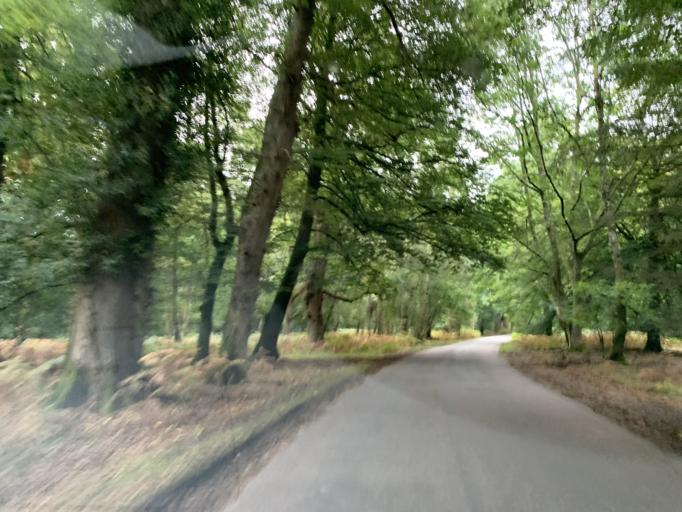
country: GB
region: England
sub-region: Hampshire
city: Lyndhurst
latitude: 50.8540
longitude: -1.6221
